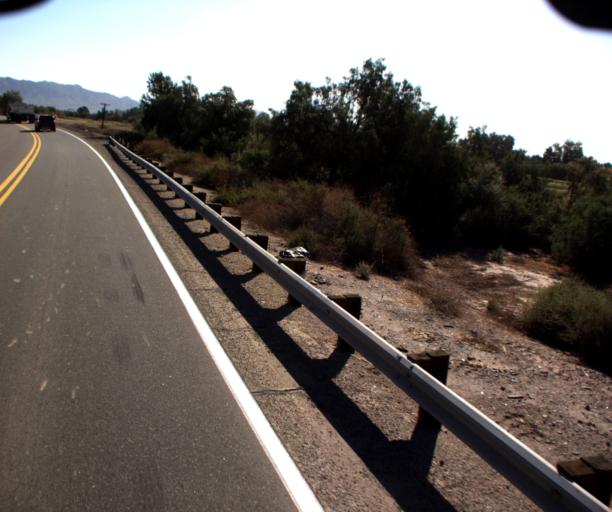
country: US
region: Arizona
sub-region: Yuma County
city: Fortuna Foothills
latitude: 32.7696
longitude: -114.3924
